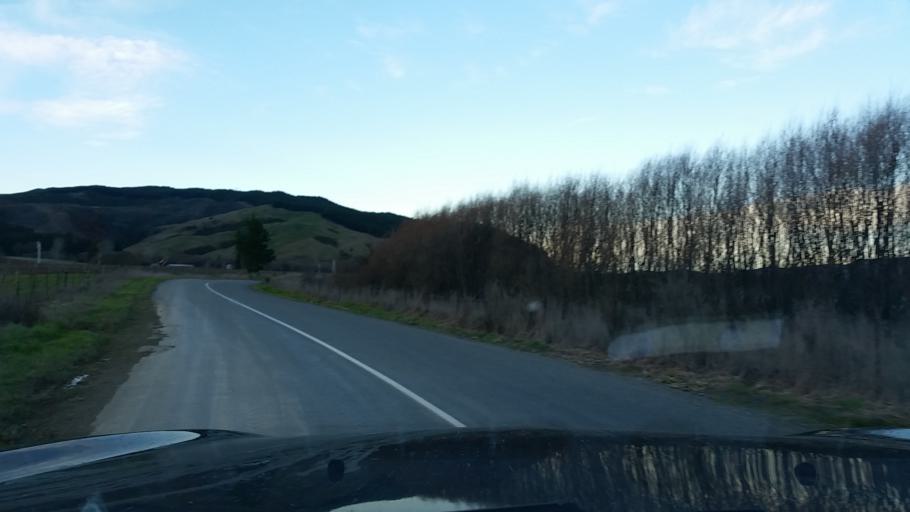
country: NZ
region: Marlborough
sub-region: Marlborough District
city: Blenheim
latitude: -41.5208
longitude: 173.5821
